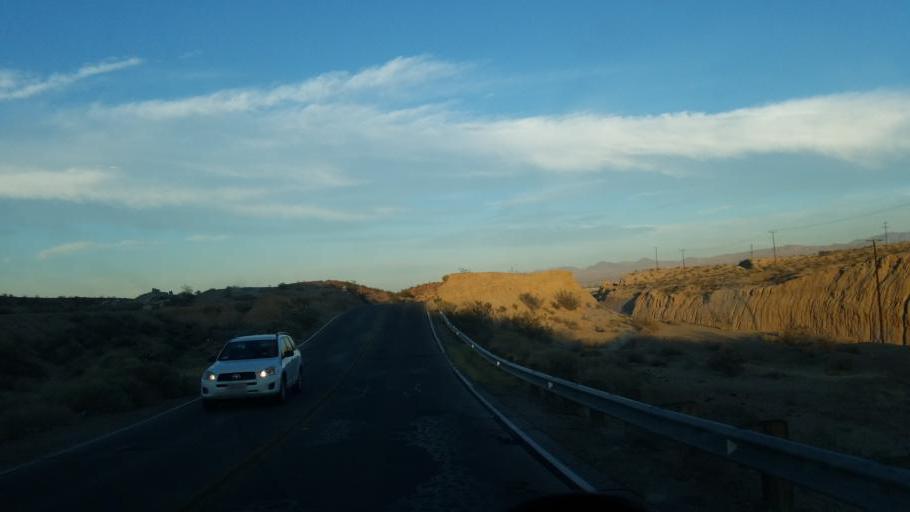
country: US
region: California
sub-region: San Bernardino County
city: Barstow
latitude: 34.9030
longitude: -117.0101
